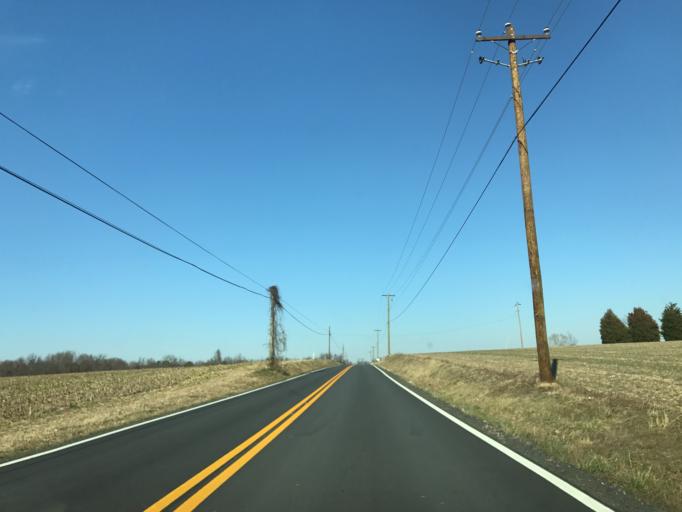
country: US
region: Maryland
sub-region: Queen Anne's County
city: Centreville
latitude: 39.0126
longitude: -76.1284
